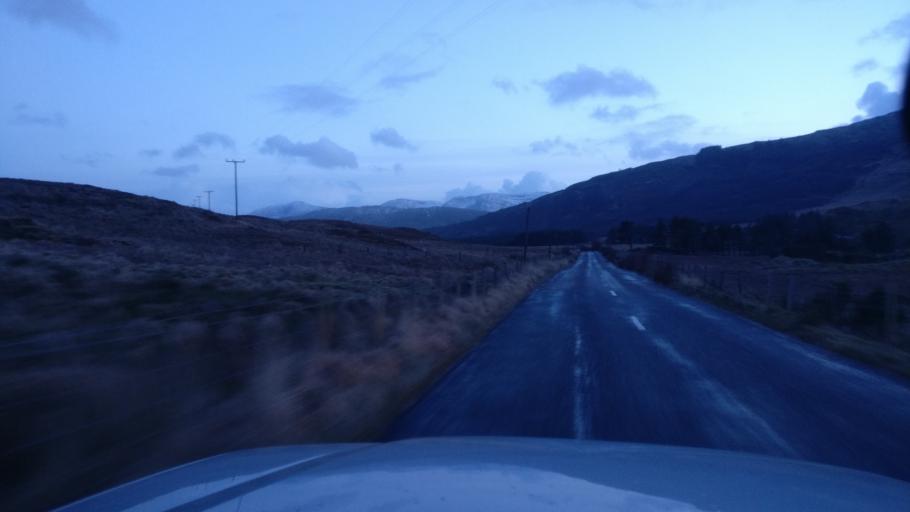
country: IE
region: Connaught
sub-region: Maigh Eo
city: Westport
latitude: 53.5622
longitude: -9.6487
